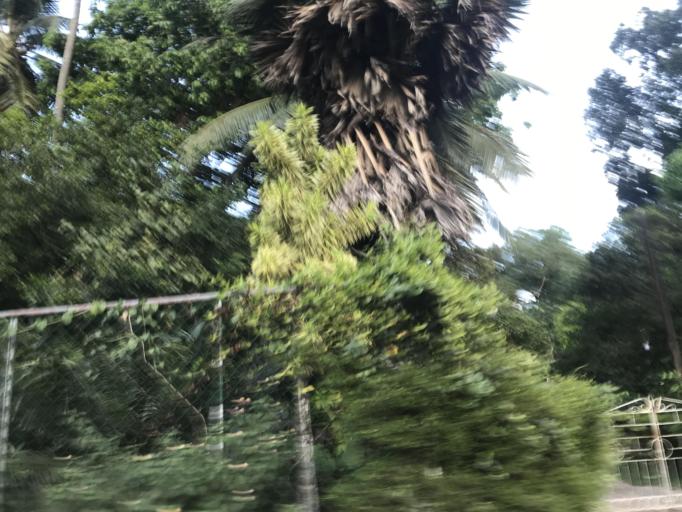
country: LK
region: Western
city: Gampaha
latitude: 7.1032
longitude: 79.9907
